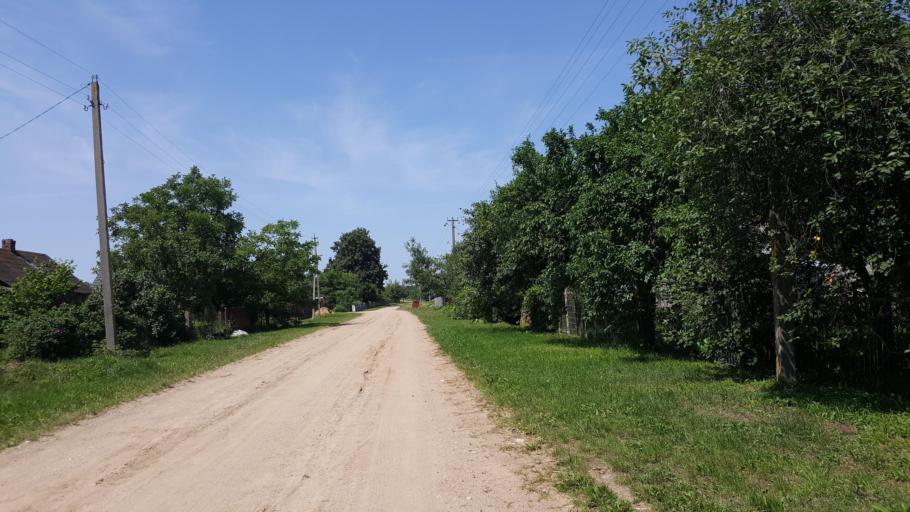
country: BY
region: Brest
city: Vysokaye
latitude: 52.3530
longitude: 23.4423
